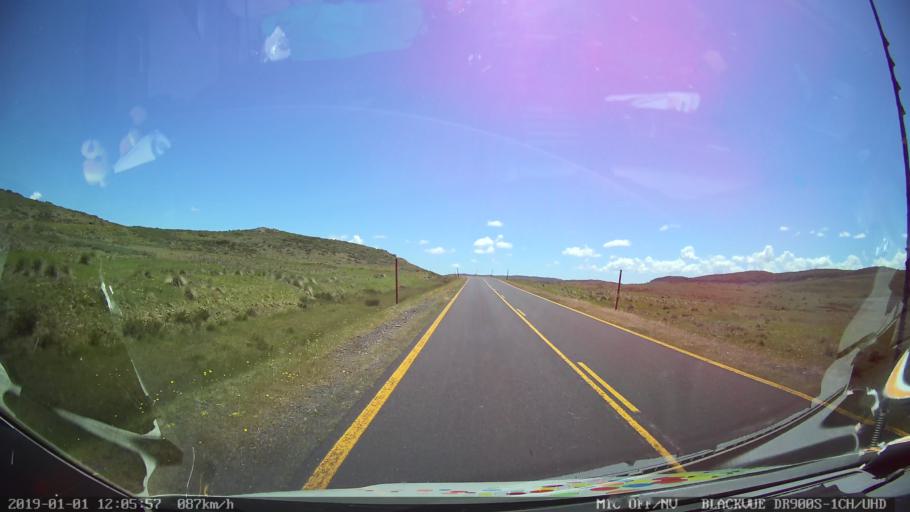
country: AU
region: New South Wales
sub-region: Snowy River
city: Jindabyne
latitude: -35.8508
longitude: 148.4908
